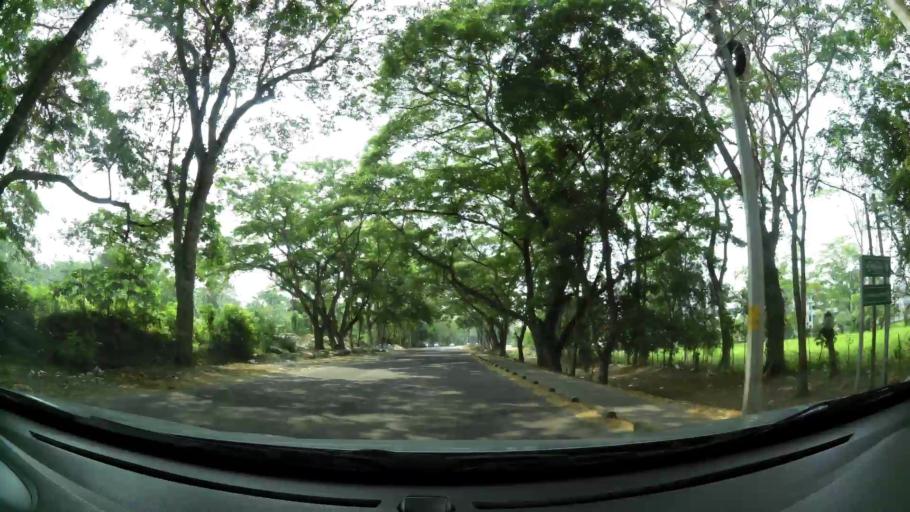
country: HN
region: Cortes
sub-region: San Pedro Sula
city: Pena Blanca
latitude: 15.5646
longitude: -88.0237
